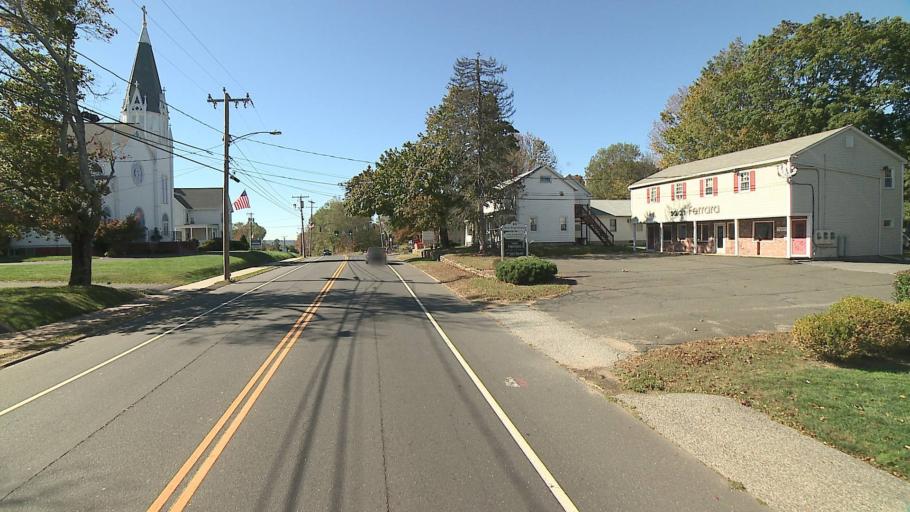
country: US
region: Connecticut
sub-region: Middlesex County
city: East Hampton
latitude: 41.5797
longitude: -72.5105
